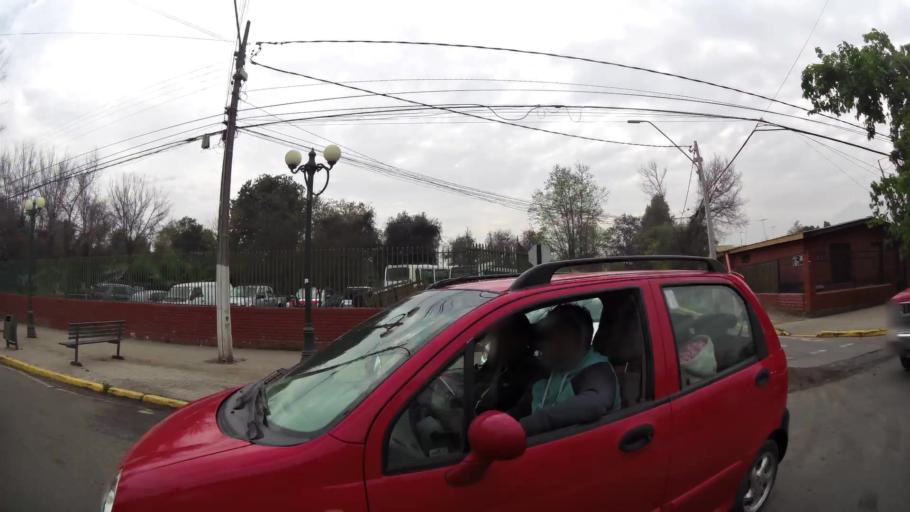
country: CL
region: Santiago Metropolitan
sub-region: Provincia de Chacabuco
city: Chicureo Abajo
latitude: -33.2046
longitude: -70.6725
